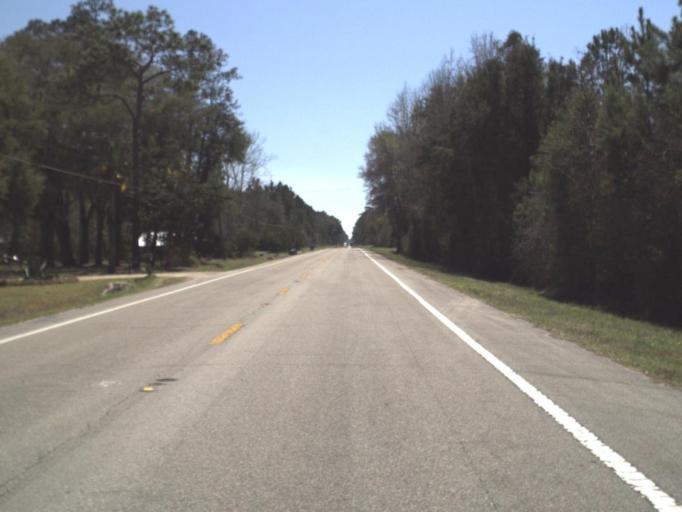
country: US
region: Florida
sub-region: Leon County
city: Woodville
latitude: 30.2209
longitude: -84.2260
